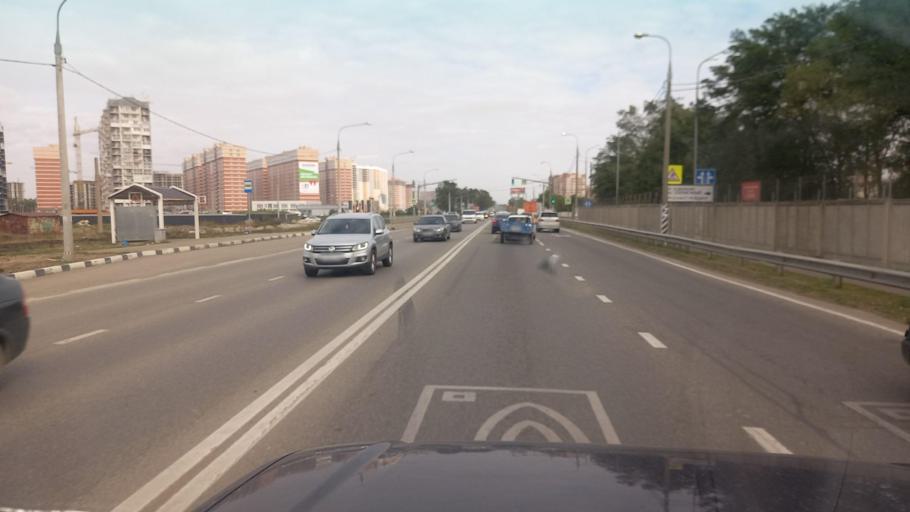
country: RU
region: Krasnodarskiy
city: Krasnodar
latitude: 45.0877
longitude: 38.9028
